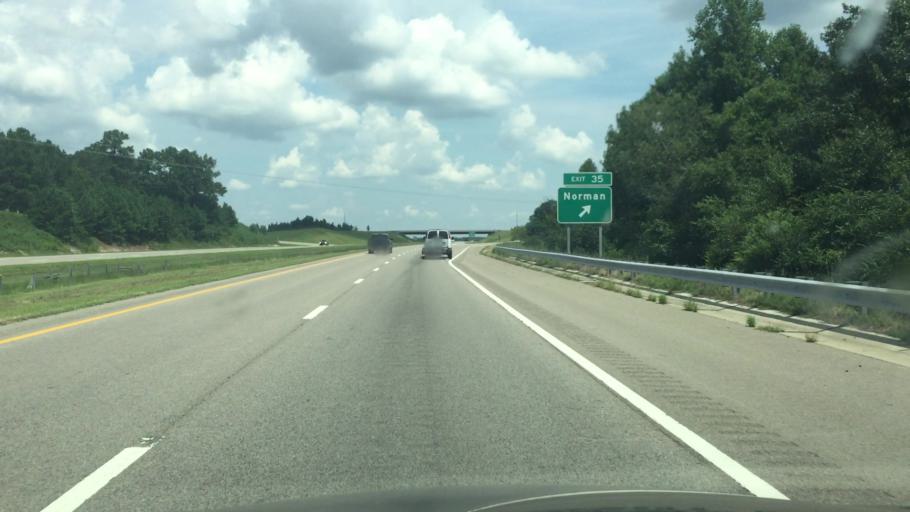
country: US
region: North Carolina
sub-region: Richmond County
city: Ellerbe
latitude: 35.1678
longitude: -79.7154
